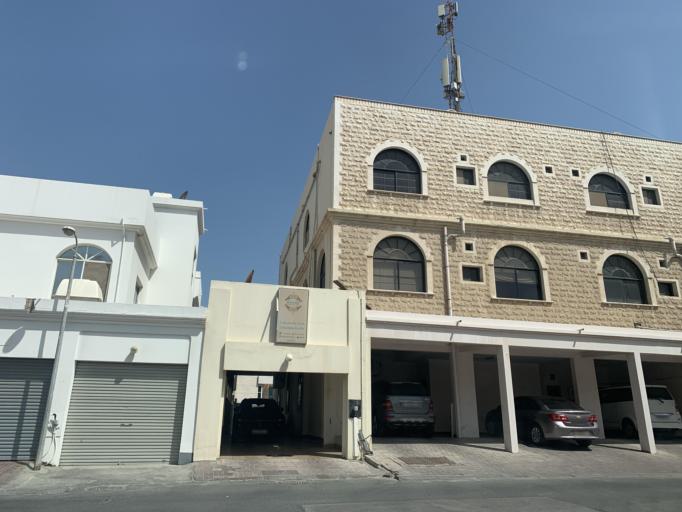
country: BH
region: Manama
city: Manama
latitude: 26.2070
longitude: 50.5817
